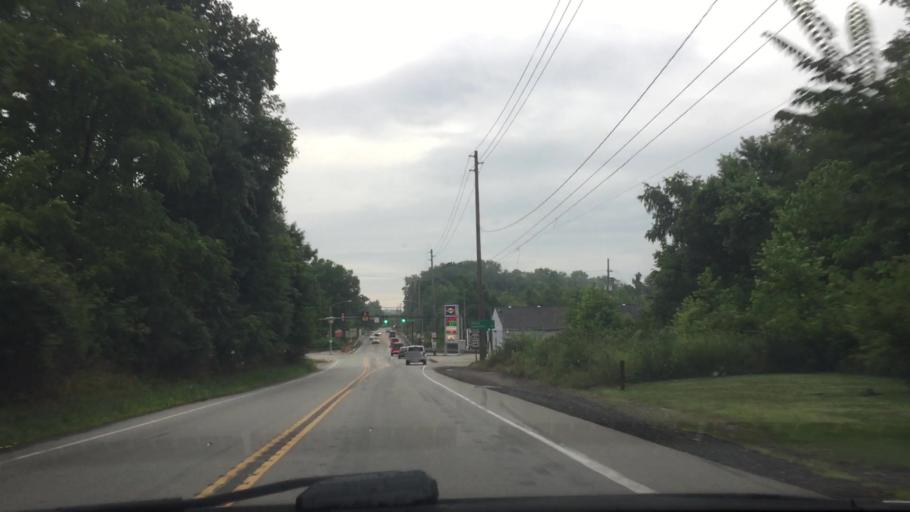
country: US
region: Pennsylvania
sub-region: Washington County
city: McGovern
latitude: 40.1825
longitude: -80.1313
